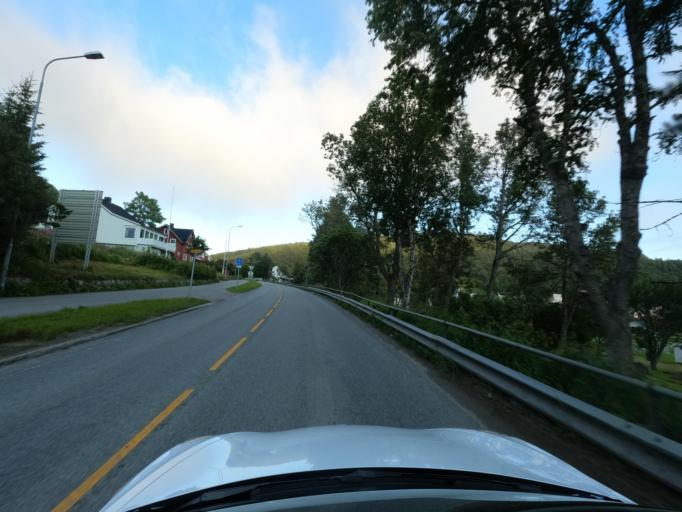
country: NO
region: Troms
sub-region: Harstad
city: Harstad
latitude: 68.8066
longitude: 16.5108
